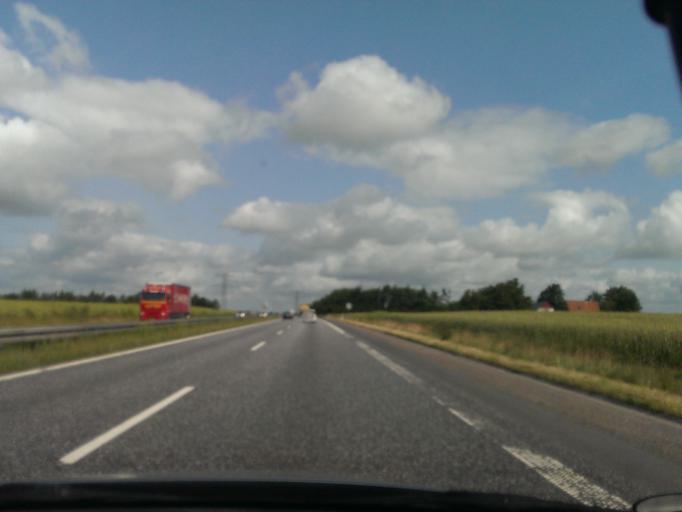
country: DK
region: Central Jutland
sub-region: Randers Kommune
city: Randers
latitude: 56.4967
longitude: 9.9792
